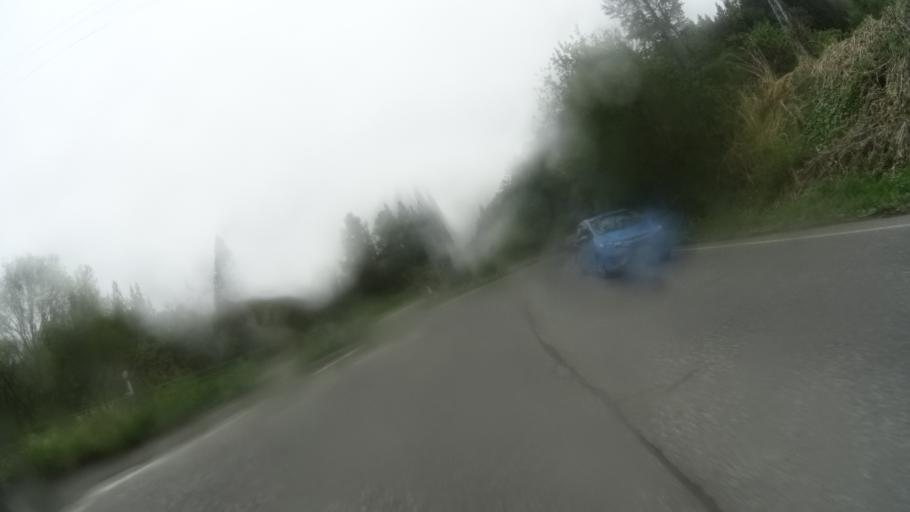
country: JP
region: Nagano
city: Nakano
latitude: 36.7206
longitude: 138.4458
